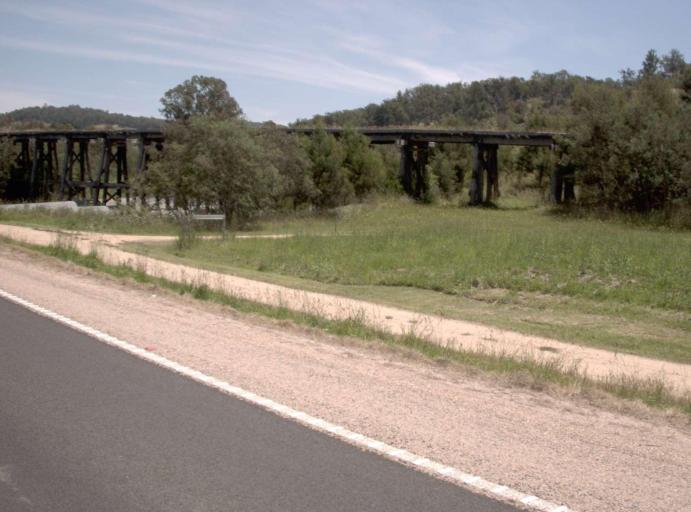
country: AU
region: Victoria
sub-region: East Gippsland
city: Bairnsdale
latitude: -37.7107
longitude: 147.8132
